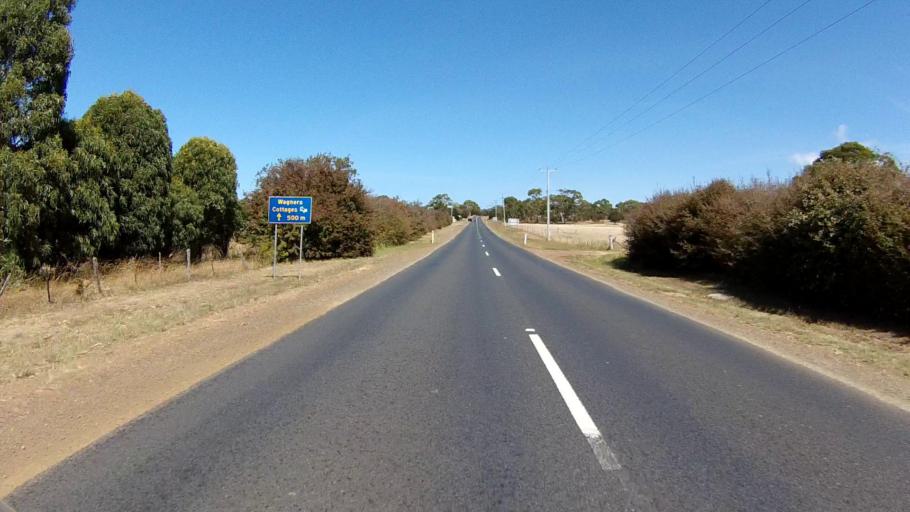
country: AU
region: Tasmania
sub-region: Sorell
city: Sorell
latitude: -42.1354
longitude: 148.0712
